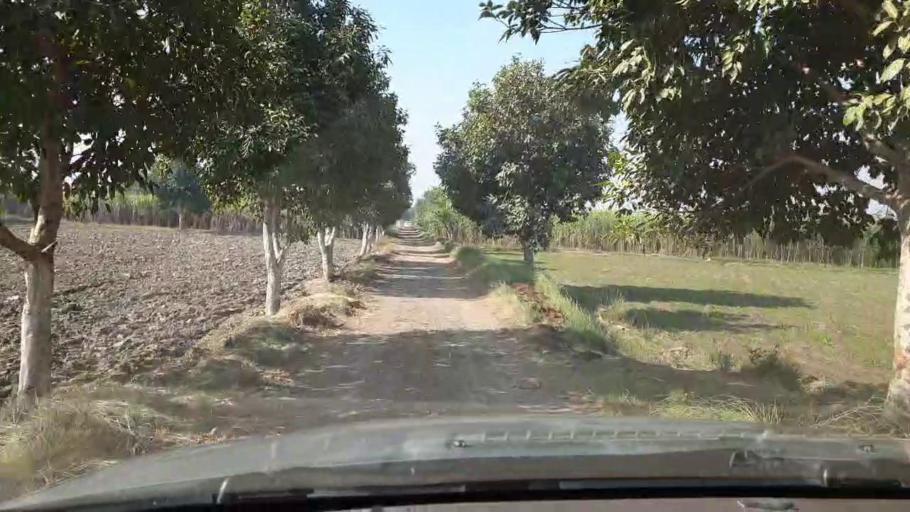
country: PK
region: Sindh
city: Tando Muhammad Khan
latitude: 25.0389
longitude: 68.5645
